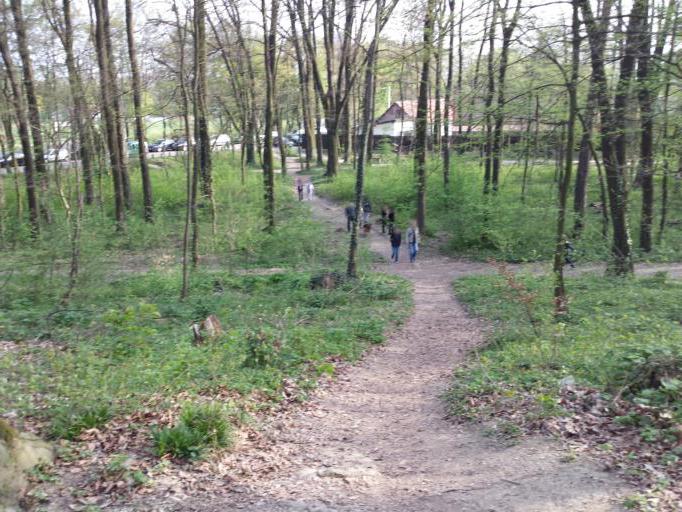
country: HR
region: Grad Zagreb
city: Dubrava
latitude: 45.8242
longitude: 16.0249
